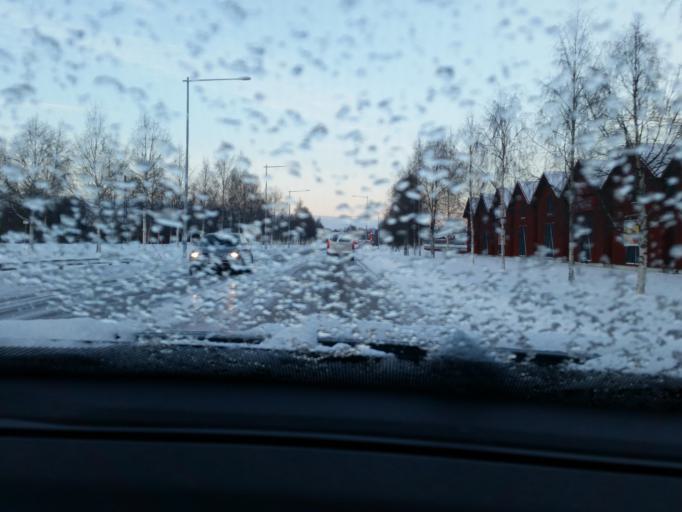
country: SE
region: Norrbotten
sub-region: Pitea Kommun
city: Pitea
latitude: 65.3135
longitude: 21.4817
